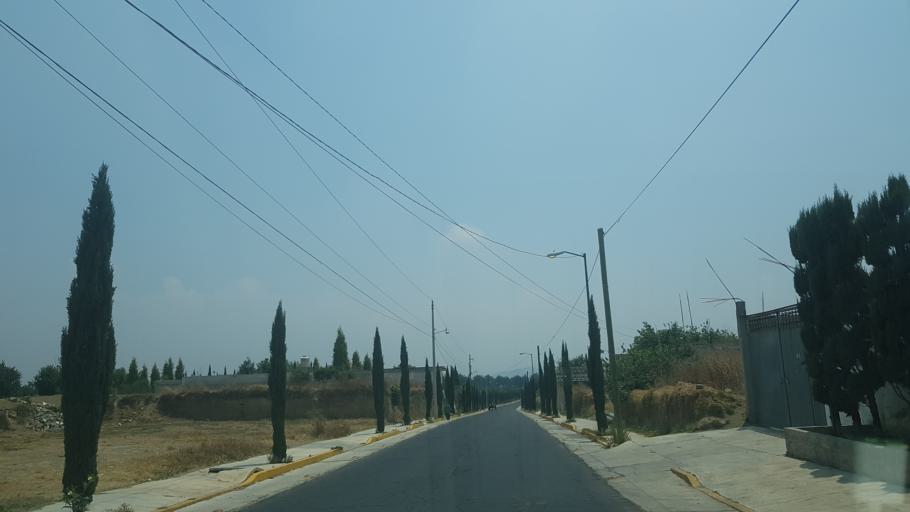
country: MX
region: Puebla
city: San Andres Calpan
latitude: 19.1035
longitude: -98.4485
